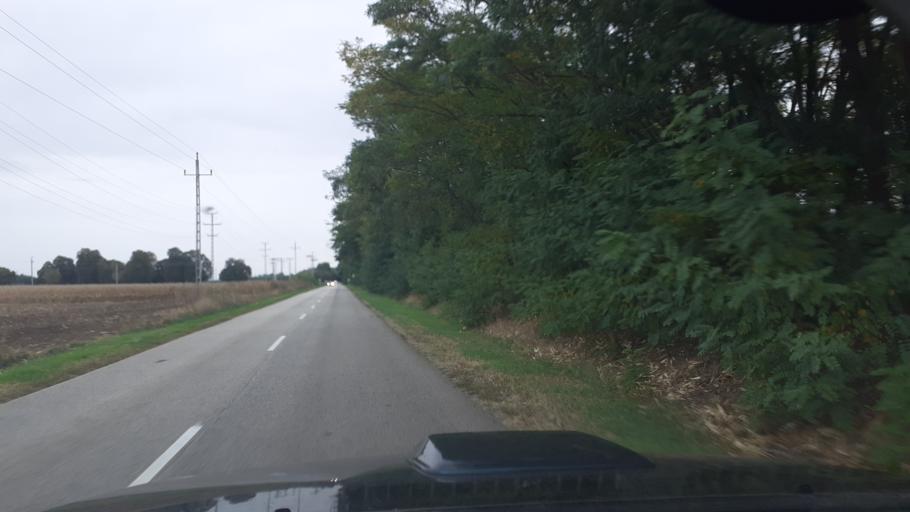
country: HU
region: Fejer
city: Baracs
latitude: 46.8400
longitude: 18.8945
